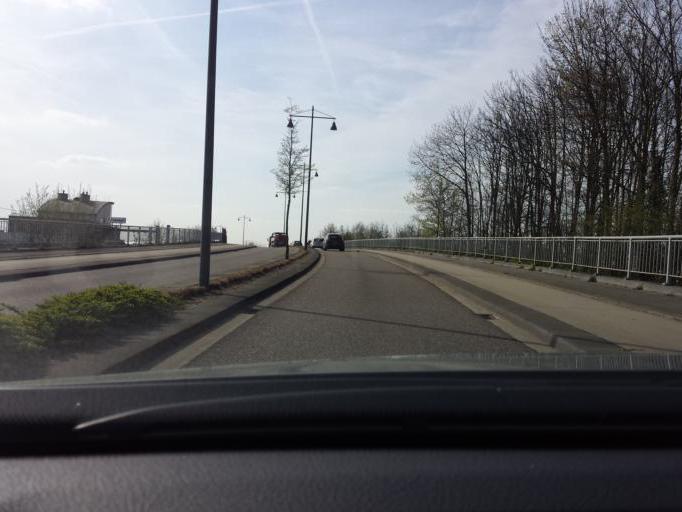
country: BE
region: Flanders
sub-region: Provincie Limburg
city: Hasselt
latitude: 50.9448
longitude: 5.2724
